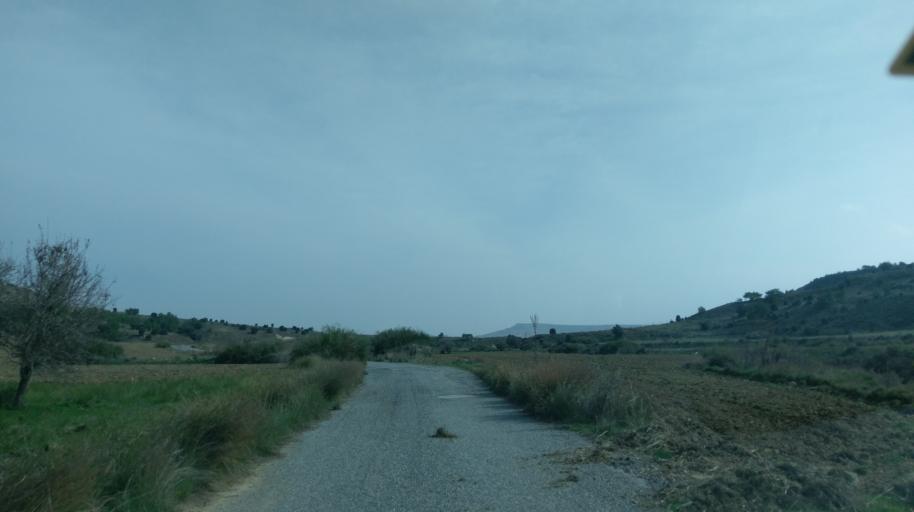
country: CY
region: Lefkosia
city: Morfou
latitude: 35.2503
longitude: 33.0574
